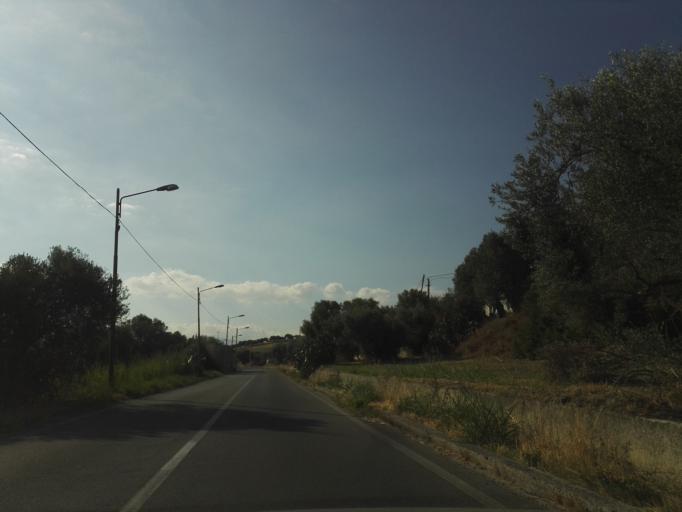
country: IT
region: Calabria
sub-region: Provincia di Reggio Calabria
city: Monasterace
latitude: 38.4413
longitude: 16.5434
